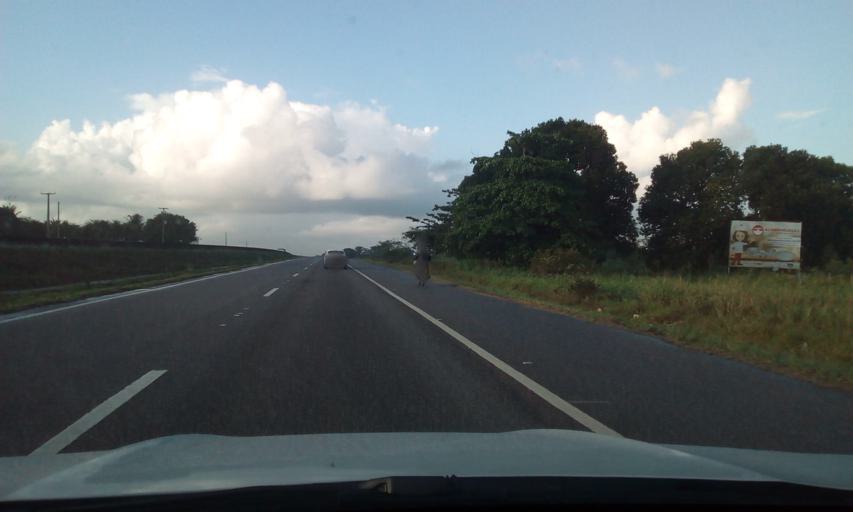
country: BR
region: Pernambuco
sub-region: Itapissuma
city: Itapissuma
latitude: -7.7035
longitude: -34.9247
